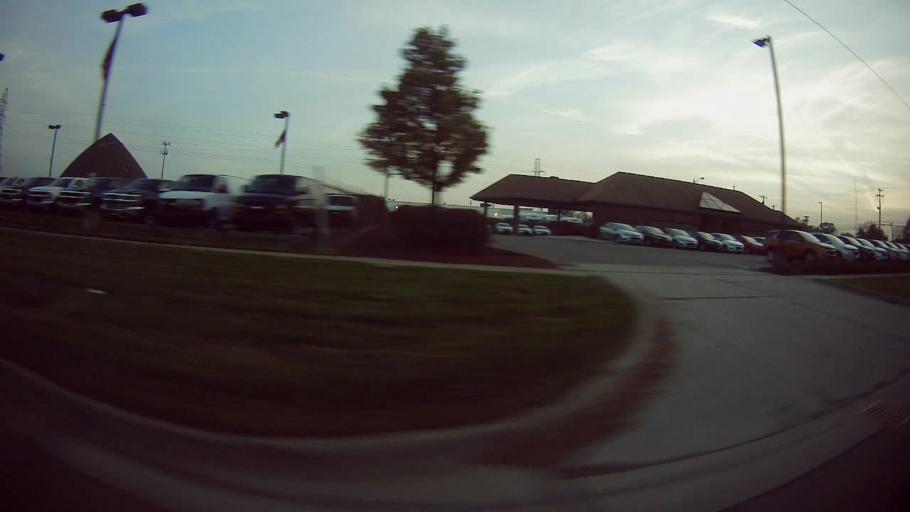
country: US
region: Michigan
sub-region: Oakland County
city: Royal Oak
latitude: 42.5042
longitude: -83.1240
